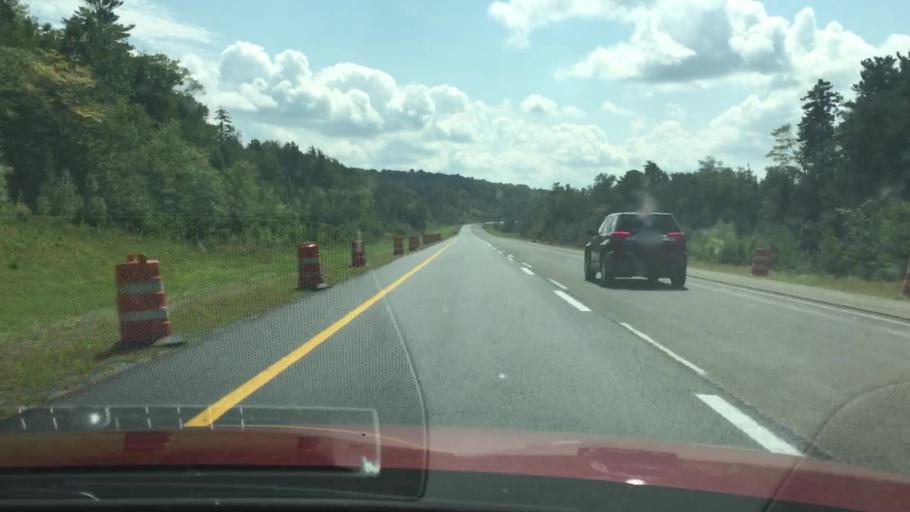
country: US
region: Maine
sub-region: Penobscot County
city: Medway
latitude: 45.7175
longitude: -68.4756
